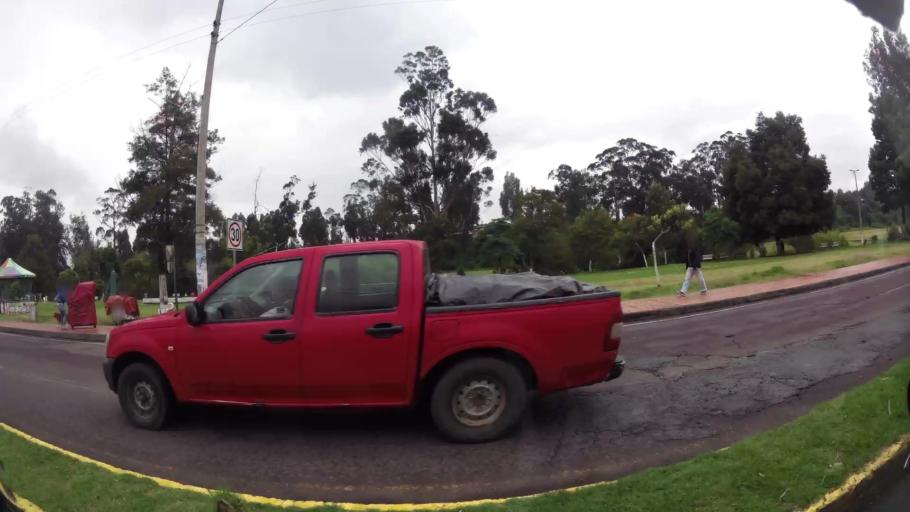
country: EC
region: Pichincha
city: Sangolqui
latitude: -0.3300
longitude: -78.4434
